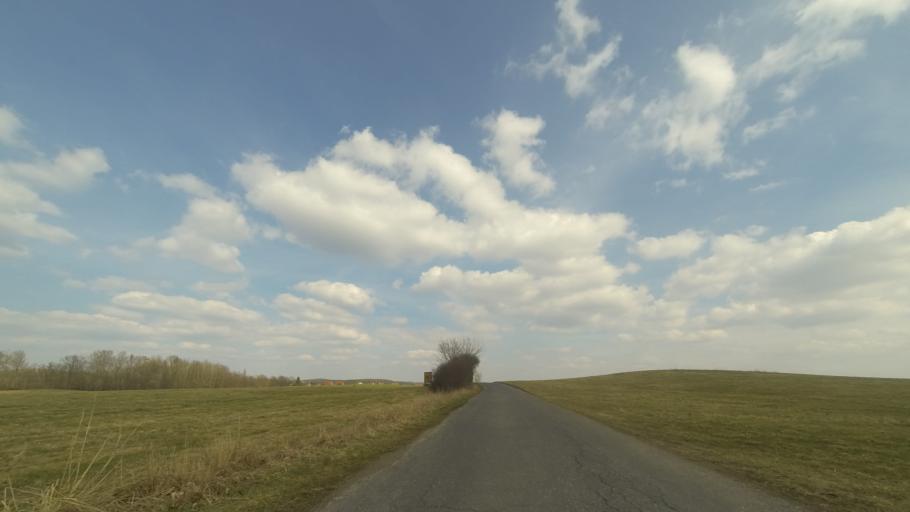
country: DE
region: Saxony
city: Moritzburg
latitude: 51.1615
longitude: 13.7165
